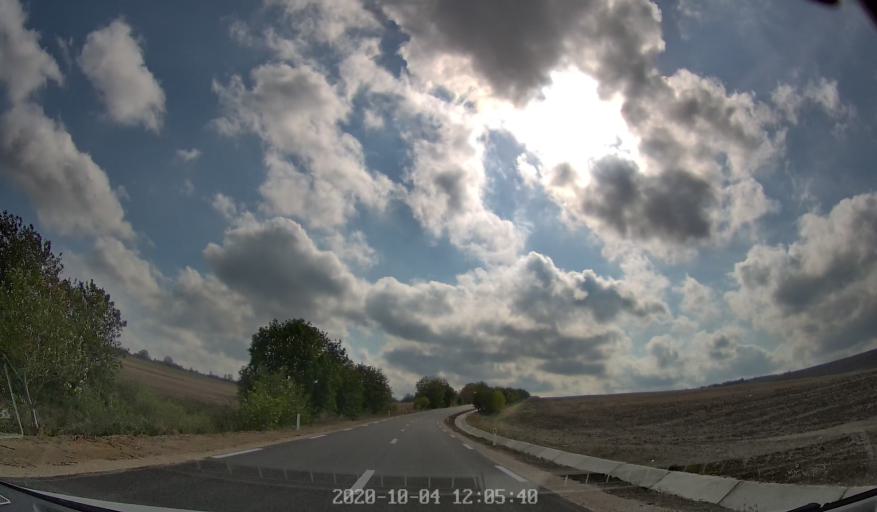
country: MD
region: Rezina
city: Saharna
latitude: 47.5919
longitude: 28.9524
